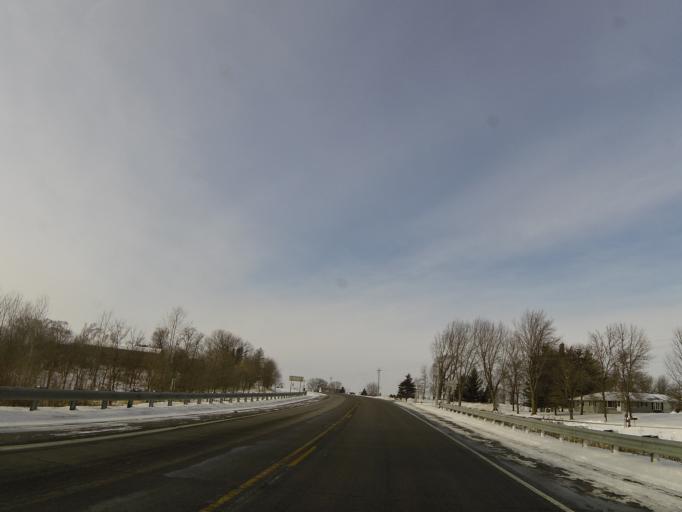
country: US
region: Minnesota
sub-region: McLeod County
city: Lester Prairie
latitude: 44.9060
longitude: -93.9761
